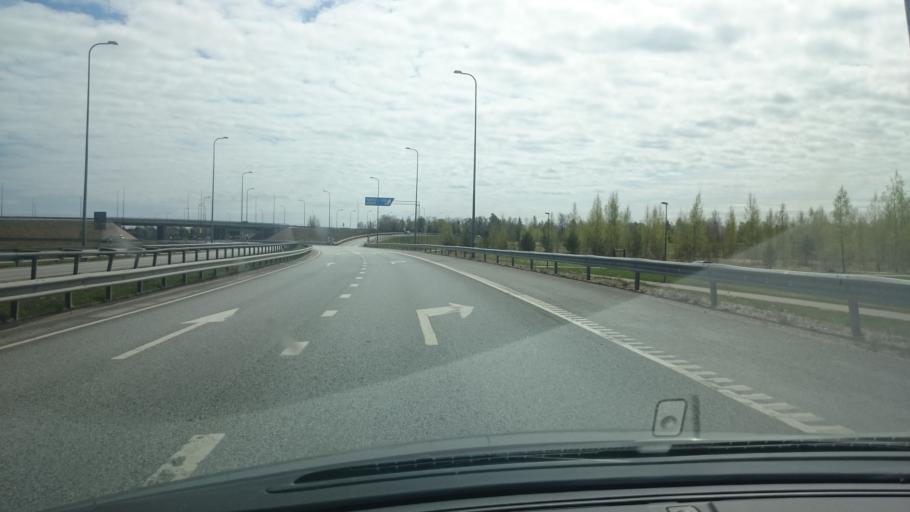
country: EE
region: Ida-Virumaa
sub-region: Johvi vald
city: Johvi
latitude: 59.3701
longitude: 27.3859
